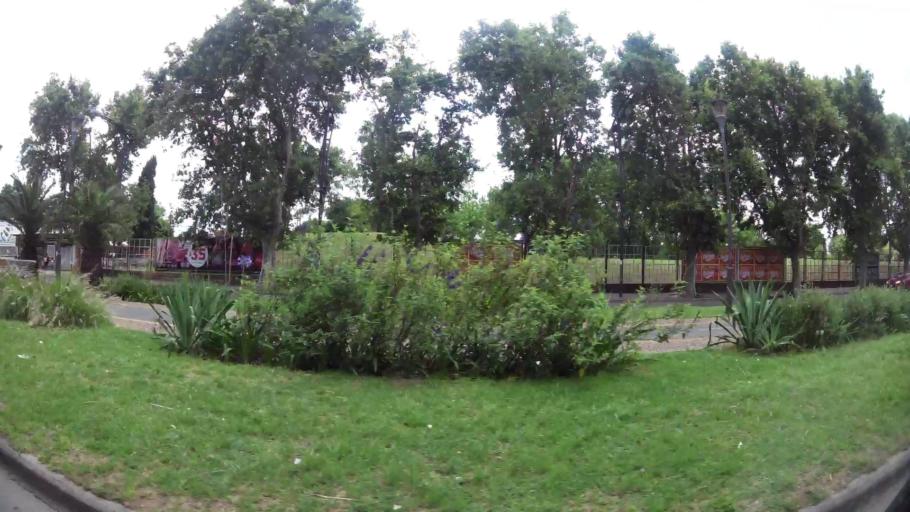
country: AR
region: Santa Fe
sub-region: Departamento de Rosario
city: Rosario
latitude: -32.9726
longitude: -60.6605
